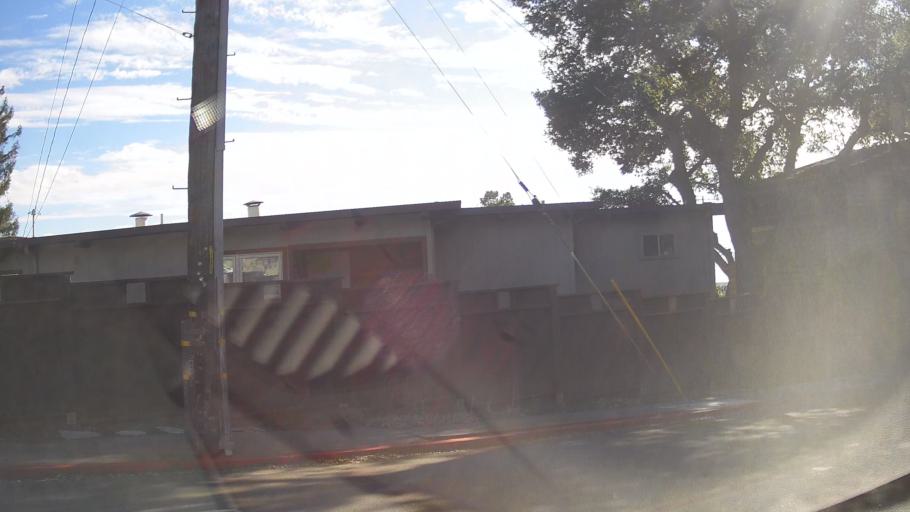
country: US
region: California
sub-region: Contra Costa County
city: Kensington
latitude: 37.8953
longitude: -122.2693
